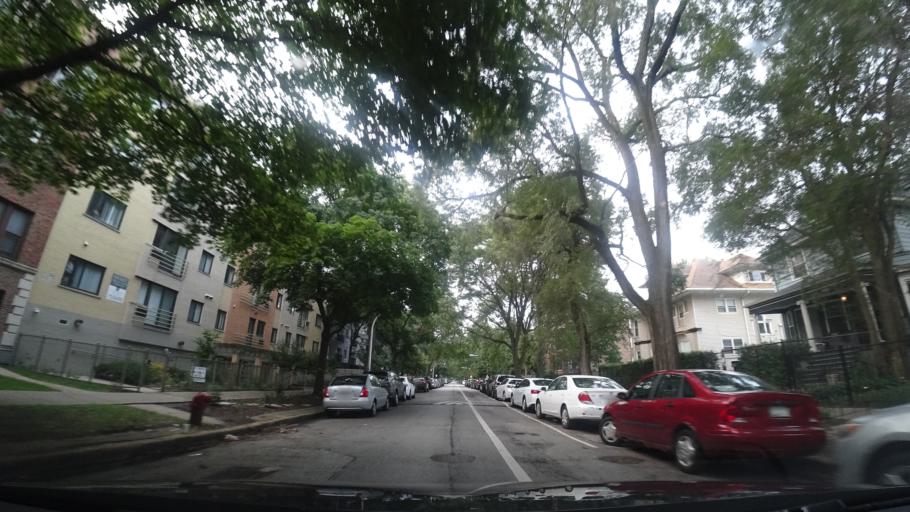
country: US
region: Illinois
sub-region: Cook County
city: Evanston
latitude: 41.9812
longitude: -87.6579
